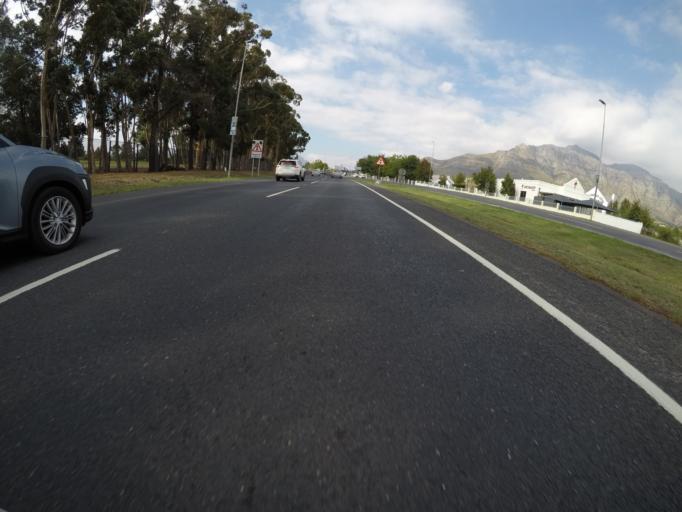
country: ZA
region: Western Cape
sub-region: Cape Winelands District Municipality
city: Stellenbosch
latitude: -33.9643
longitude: 18.8488
